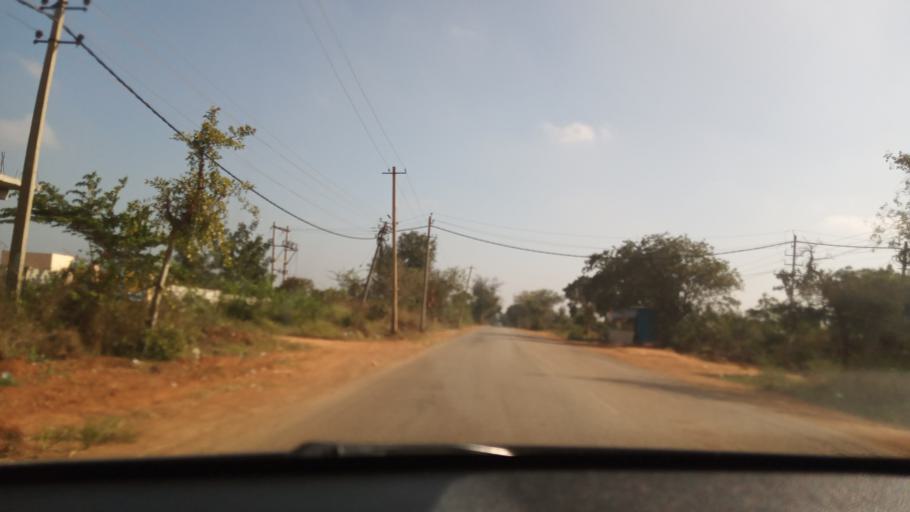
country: IN
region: Karnataka
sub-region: Bangalore Rural
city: Devanhalli
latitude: 13.2596
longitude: 77.7300
